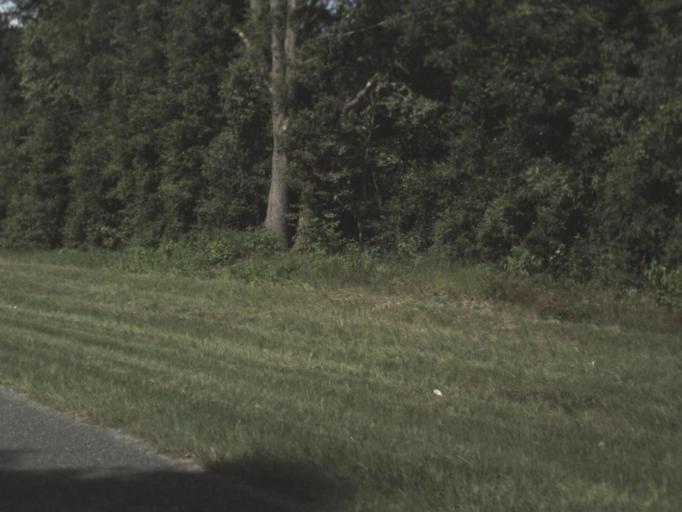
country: US
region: Florida
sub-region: Alachua County
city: High Springs
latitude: 29.9792
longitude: -82.7099
